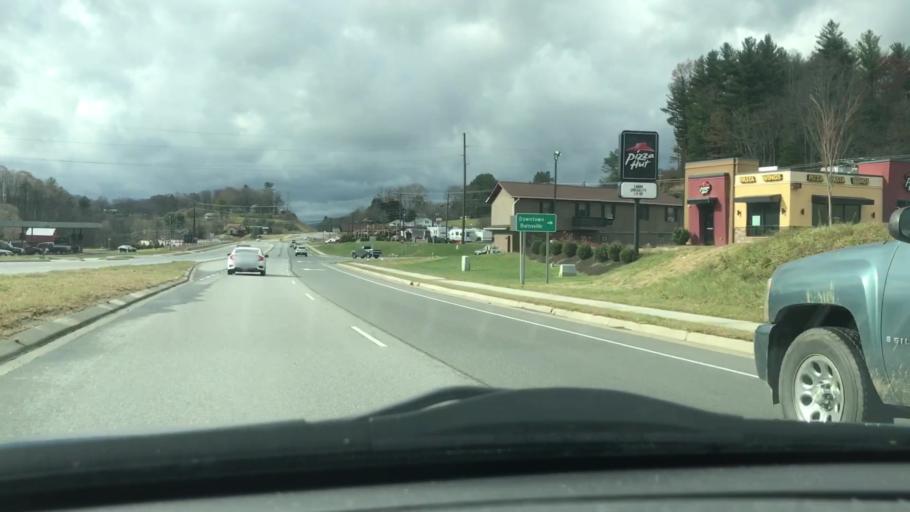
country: US
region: North Carolina
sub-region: Yancey County
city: Burnsville
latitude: 35.9127
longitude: -82.3137
